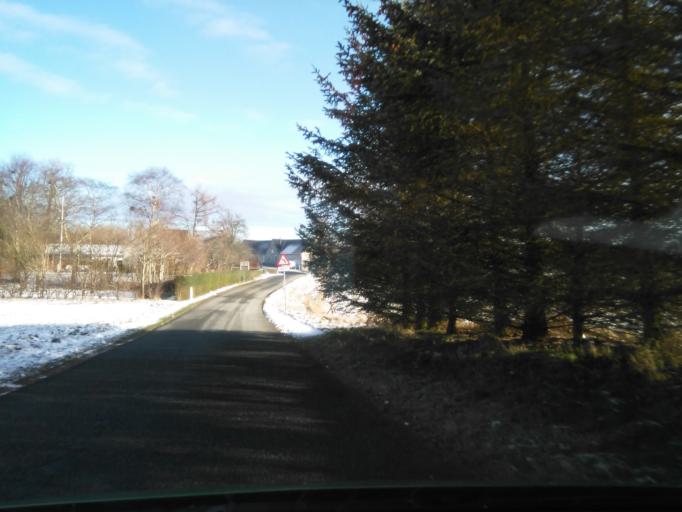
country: DK
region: Central Jutland
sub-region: Skanderborg Kommune
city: Skovby
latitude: 56.1423
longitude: 9.9604
